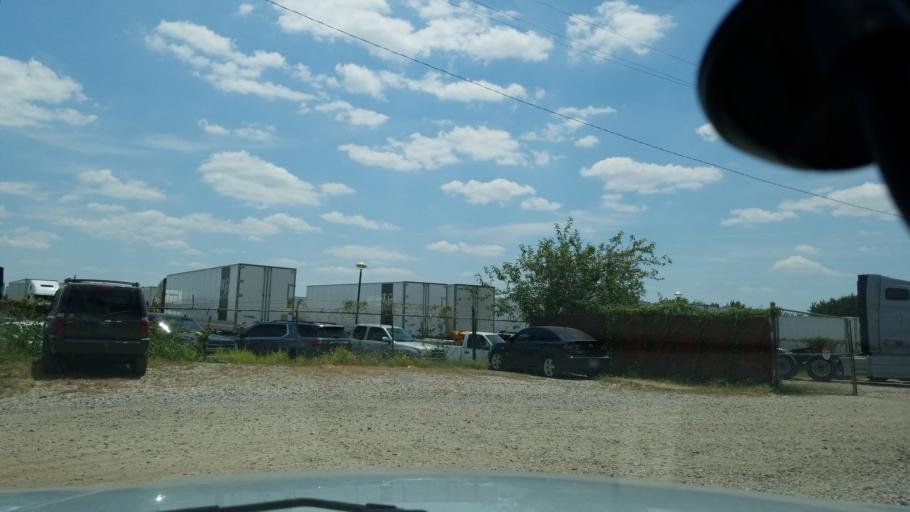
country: US
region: Texas
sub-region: Dallas County
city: Grand Prairie
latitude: 32.7479
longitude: -96.9737
